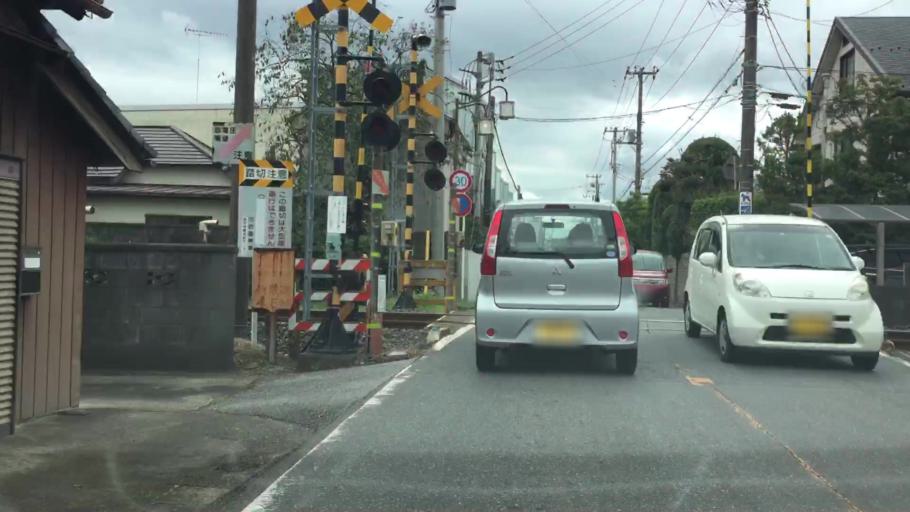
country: JP
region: Ibaraki
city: Ryugasaki
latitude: 35.8389
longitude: 140.1441
